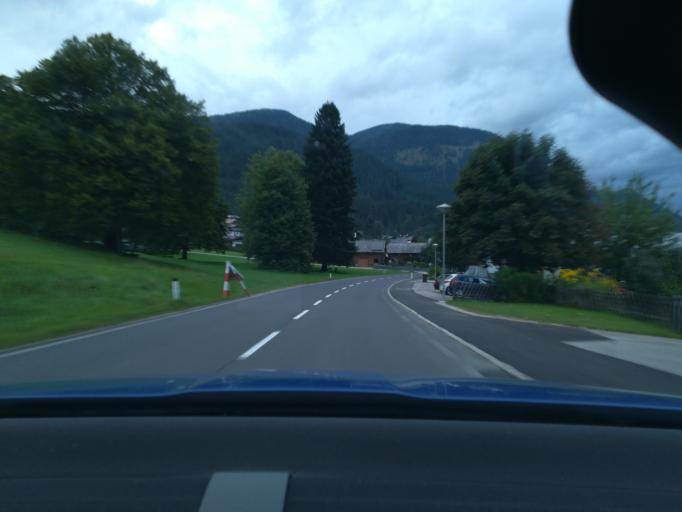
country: AT
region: Upper Austria
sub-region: Politischer Bezirk Gmunden
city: Bad Goisern
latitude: 47.5861
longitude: 13.5372
